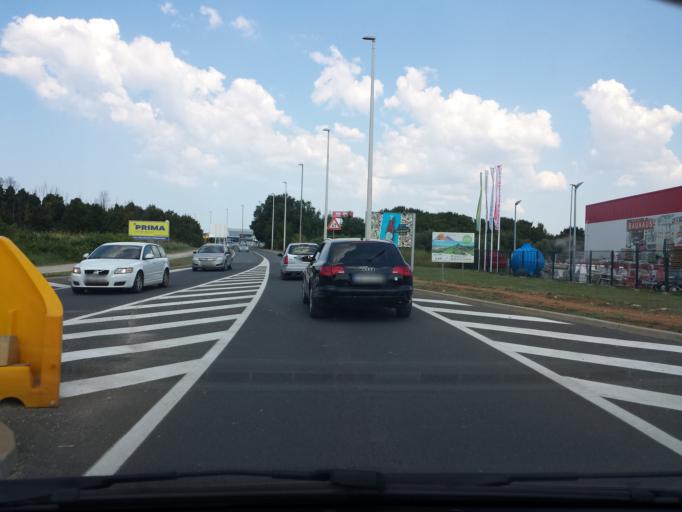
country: HR
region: Istarska
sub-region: Grad Pula
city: Pula
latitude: 44.8838
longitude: 13.8617
